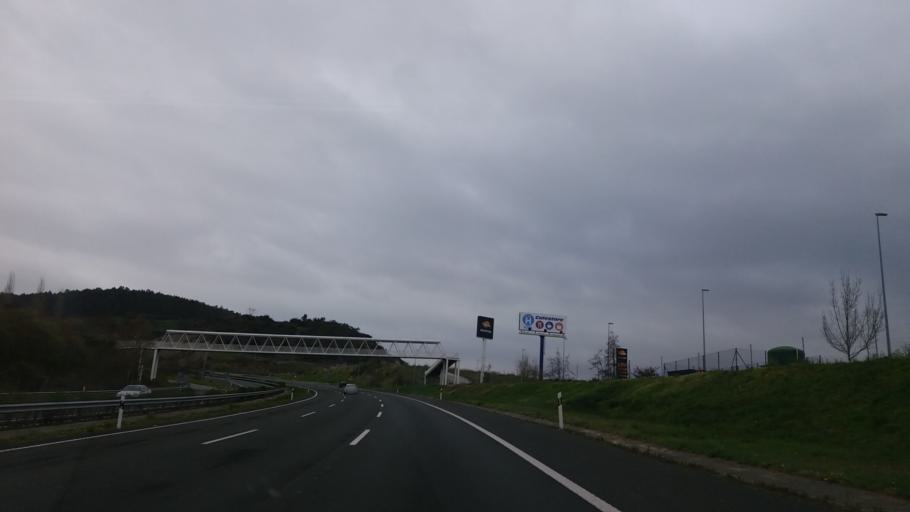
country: ES
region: Cantabria
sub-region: Provincia de Cantabria
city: Comillas
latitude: 43.3356
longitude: -4.3328
